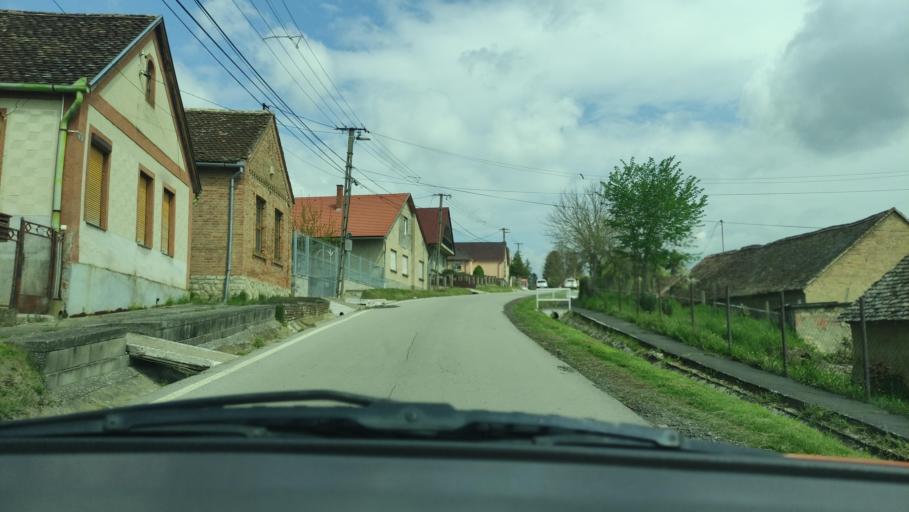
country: HU
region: Baranya
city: Sasd
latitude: 46.2876
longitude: 18.1016
